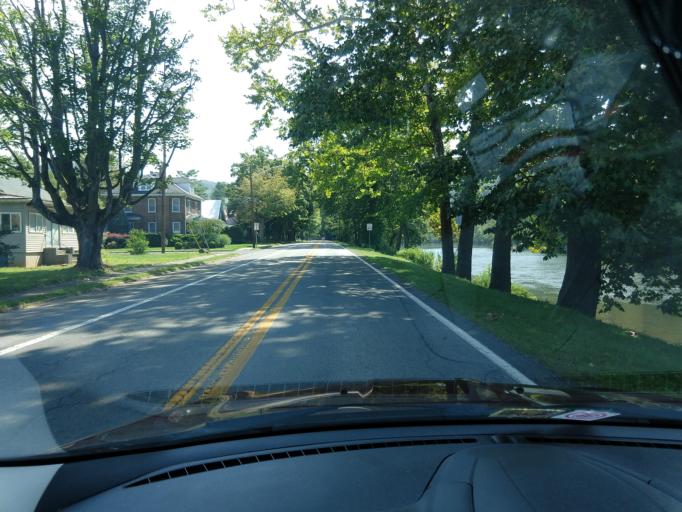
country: US
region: West Virginia
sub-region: Greenbrier County
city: Alderson
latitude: 37.7244
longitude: -80.6374
